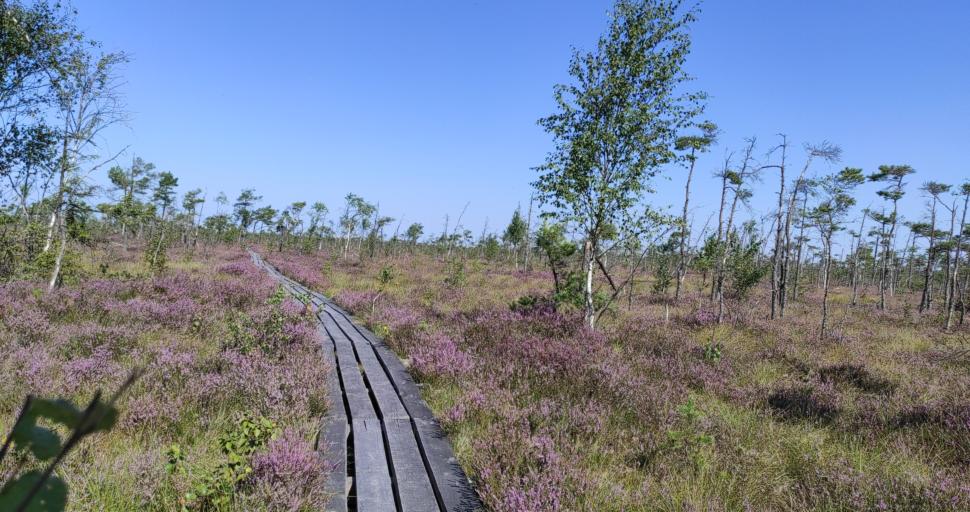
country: LT
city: Skuodas
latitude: 56.2492
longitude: 21.3958
